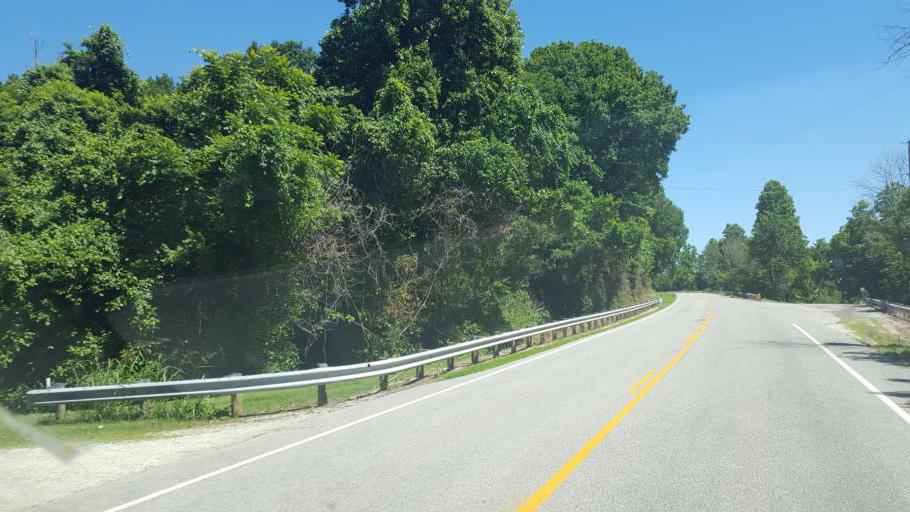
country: US
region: West Virginia
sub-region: Cabell County
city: Lesage
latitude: 38.5502
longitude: -82.2974
